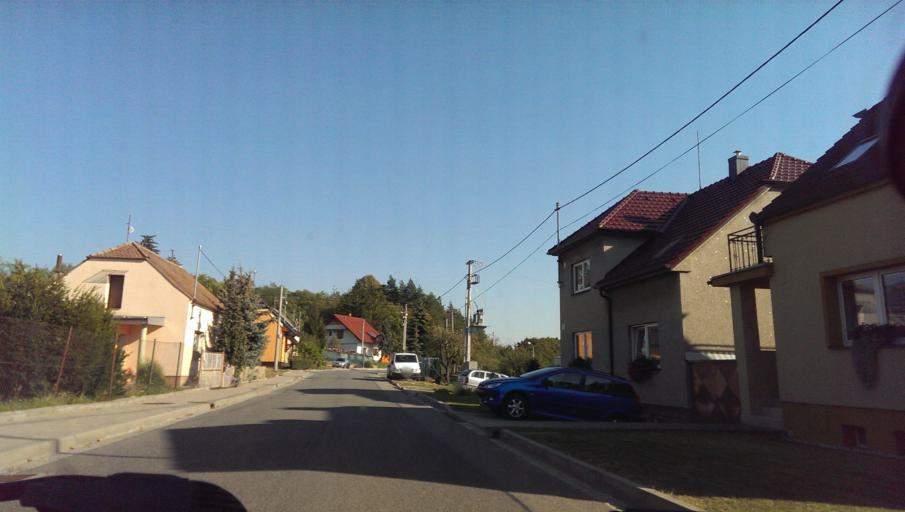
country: CZ
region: Zlin
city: Popovice
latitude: 49.0483
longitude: 17.5235
